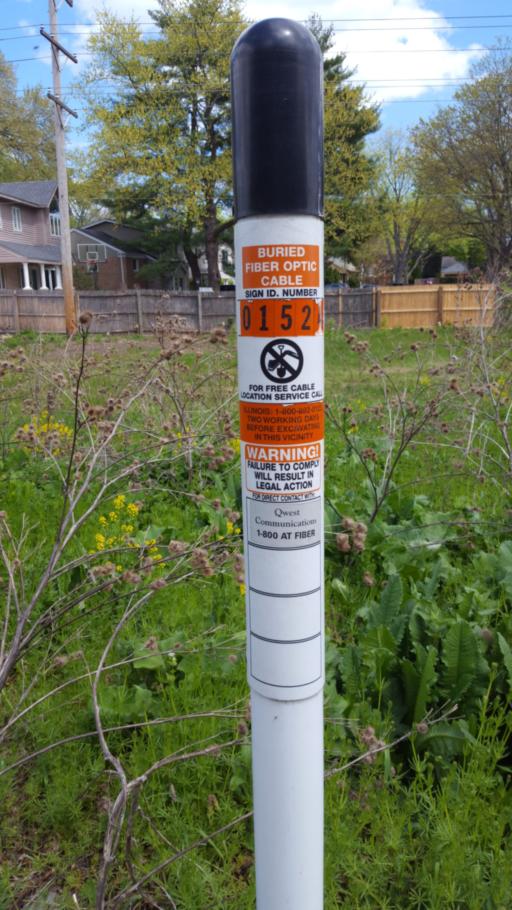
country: US
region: Illinois
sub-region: Cook County
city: Glenview
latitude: 42.0668
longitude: -87.7607
